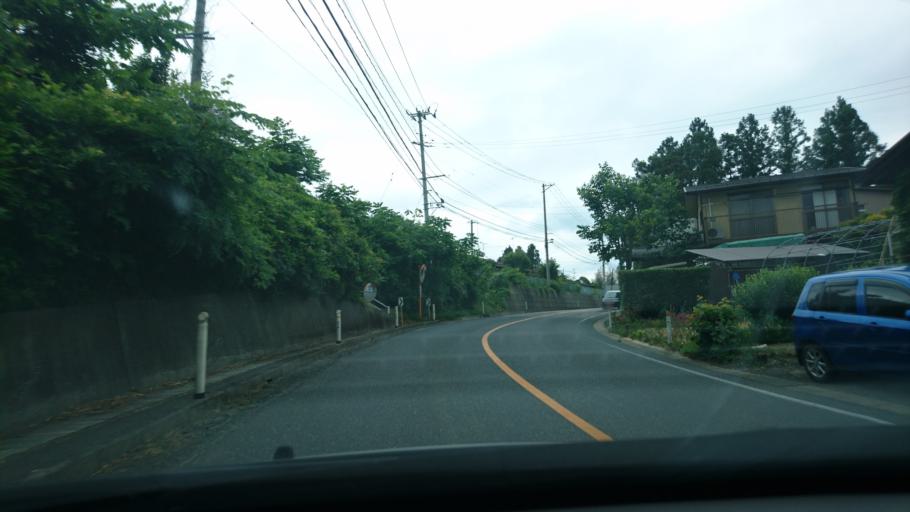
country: JP
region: Iwate
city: Ichinoseki
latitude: 38.8230
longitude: 141.1818
